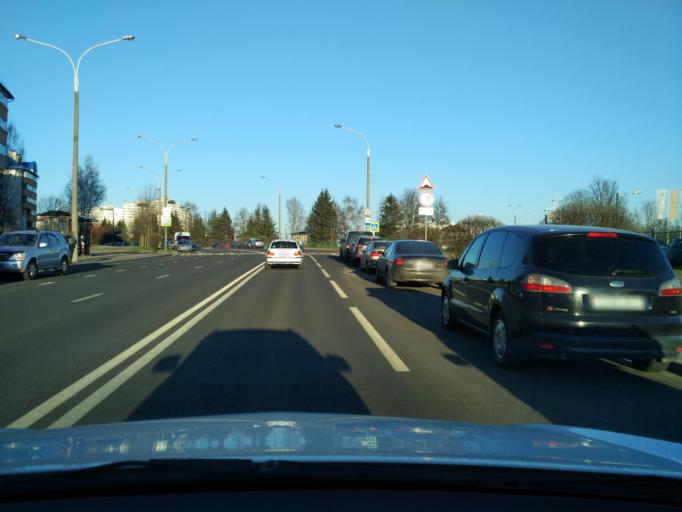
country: BY
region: Minsk
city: Shchomyslitsa
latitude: 53.8444
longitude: 27.4631
